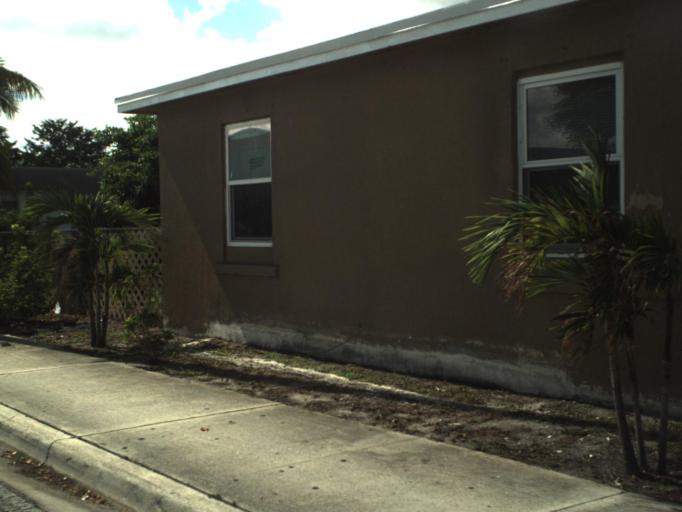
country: US
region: Florida
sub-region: Broward County
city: Dania Beach
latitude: 26.0336
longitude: -80.1479
